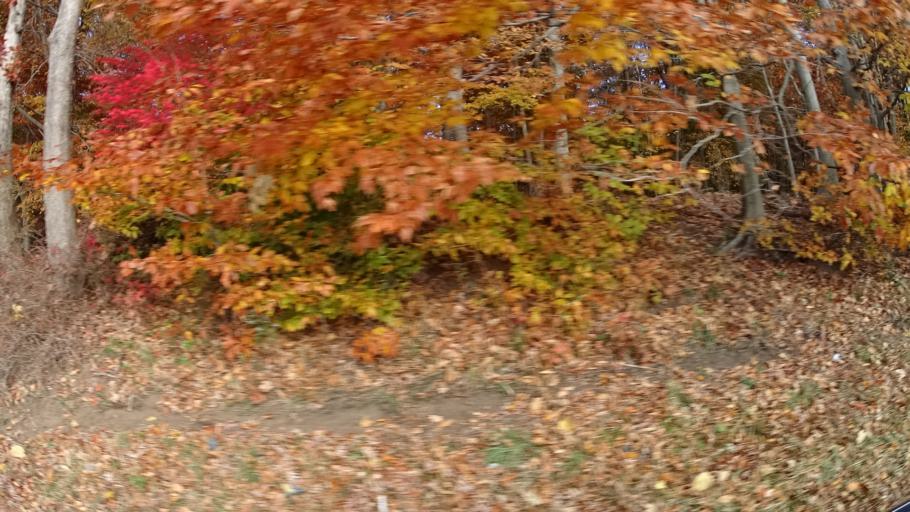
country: US
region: New Jersey
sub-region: Morris County
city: Madison
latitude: 40.7515
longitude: -74.4375
